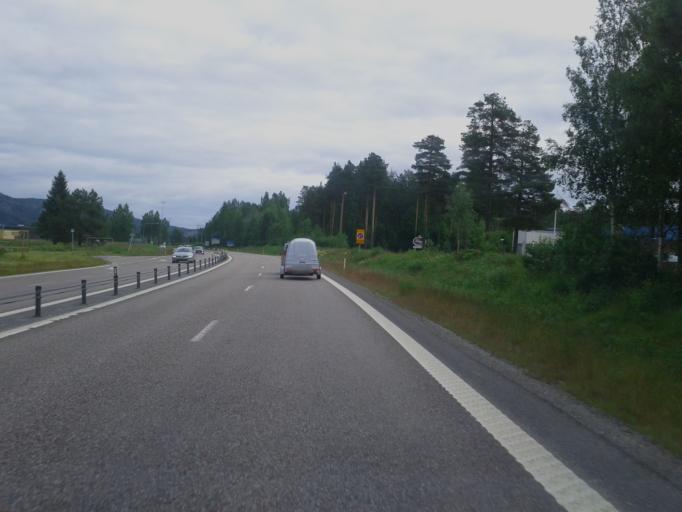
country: SE
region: Vaesternorrland
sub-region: OErnskoeldsviks Kommun
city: Ornskoldsvik
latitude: 63.2871
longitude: 18.6081
